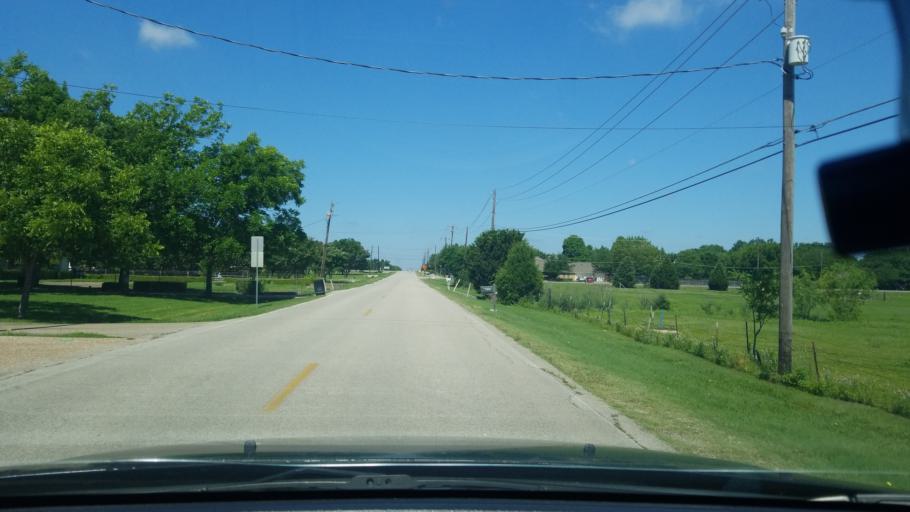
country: US
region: Texas
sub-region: Dallas County
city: Sunnyvale
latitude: 32.7961
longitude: -96.5766
